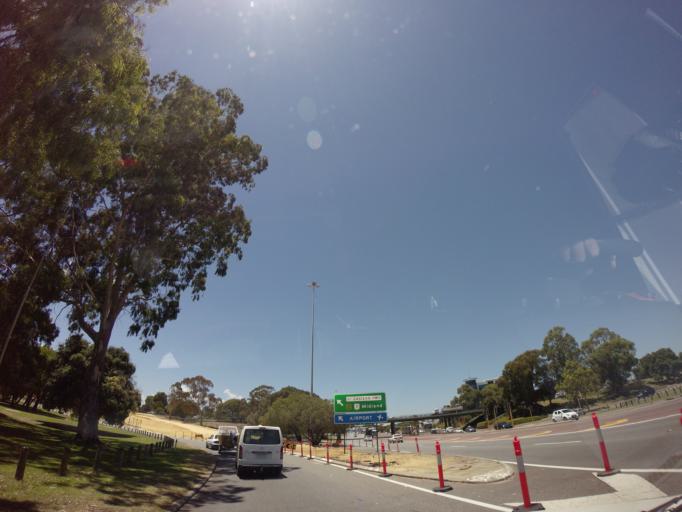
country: AU
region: Western Australia
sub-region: Belmont
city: Burswood
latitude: -31.9674
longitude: 115.8877
